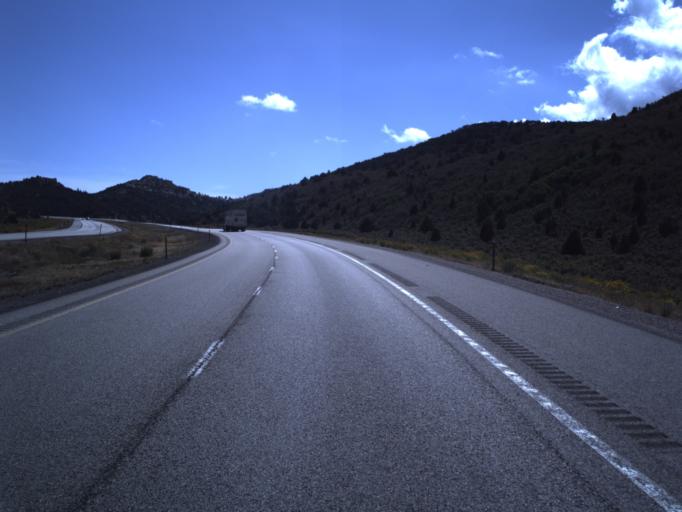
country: US
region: Utah
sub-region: Sevier County
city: Salina
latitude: 38.7899
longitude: -111.5039
